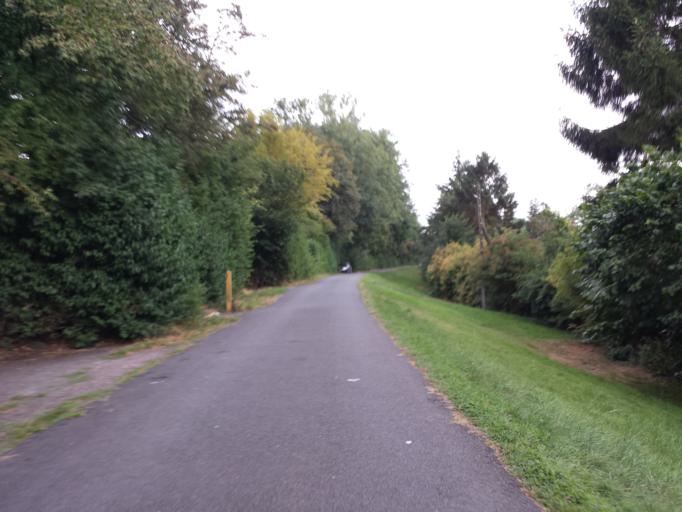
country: DE
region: Lower Saxony
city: Stuhr
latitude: 53.0649
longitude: 8.7682
